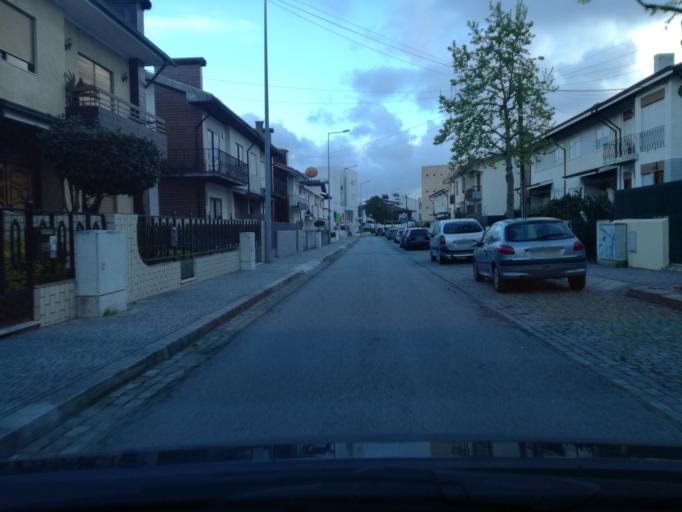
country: PT
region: Porto
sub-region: Maia
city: Gemunde
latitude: 41.2537
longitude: -8.6643
